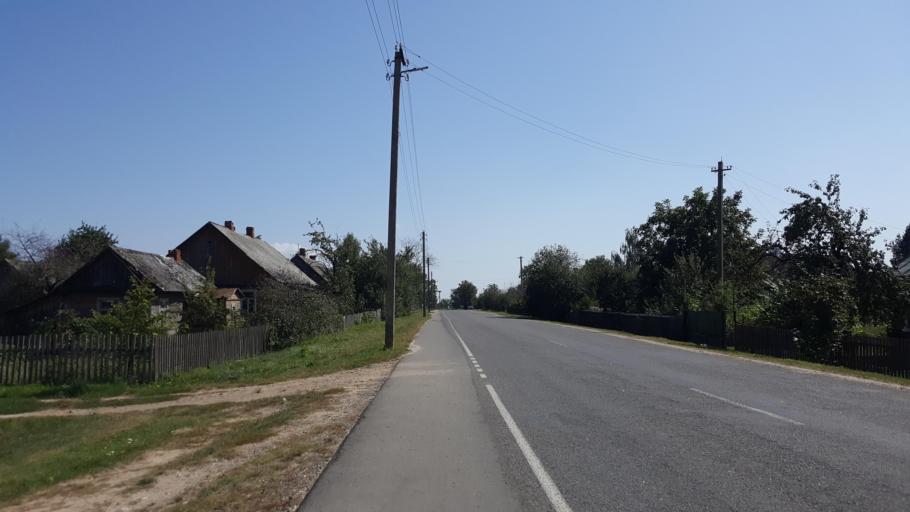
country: PL
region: Podlasie
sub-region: Powiat hajnowski
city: Czeremcha
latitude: 52.4729
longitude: 23.5079
